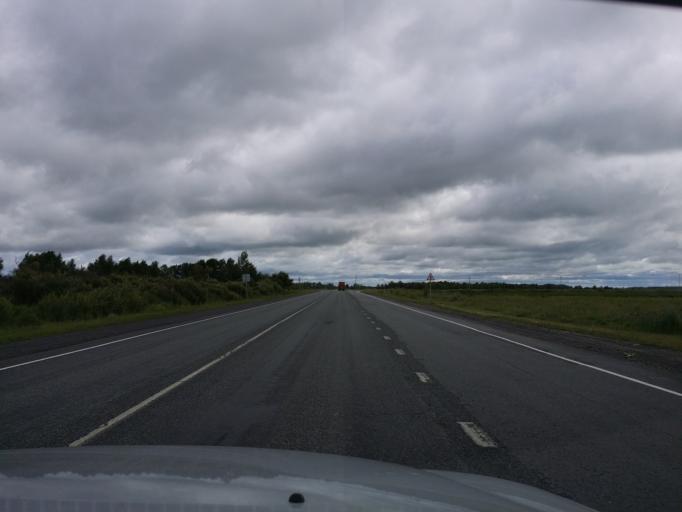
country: RU
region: Tjumen
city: Yarkovo
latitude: 57.2216
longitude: 66.6860
